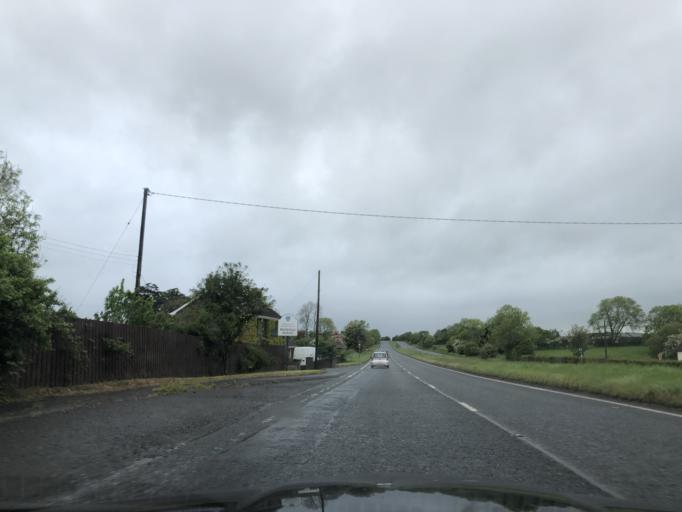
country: GB
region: Northern Ireland
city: Connor
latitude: 54.7961
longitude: -6.2559
